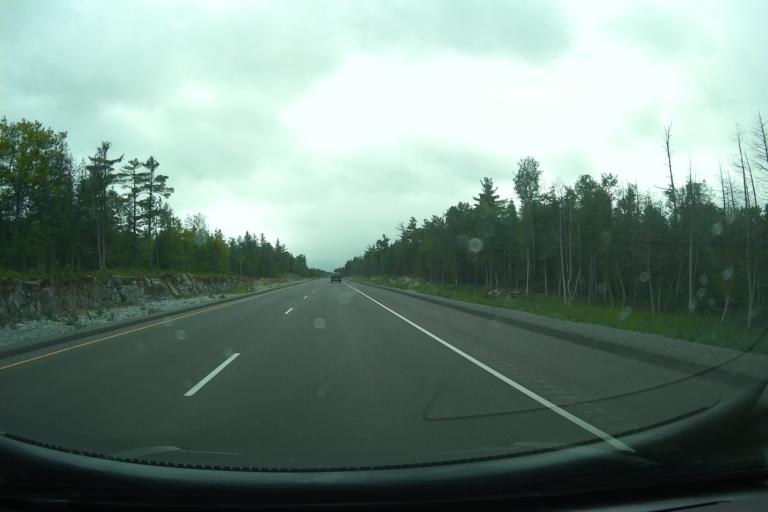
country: CA
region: Ontario
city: Arnprior
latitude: 45.4368
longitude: -76.4283
